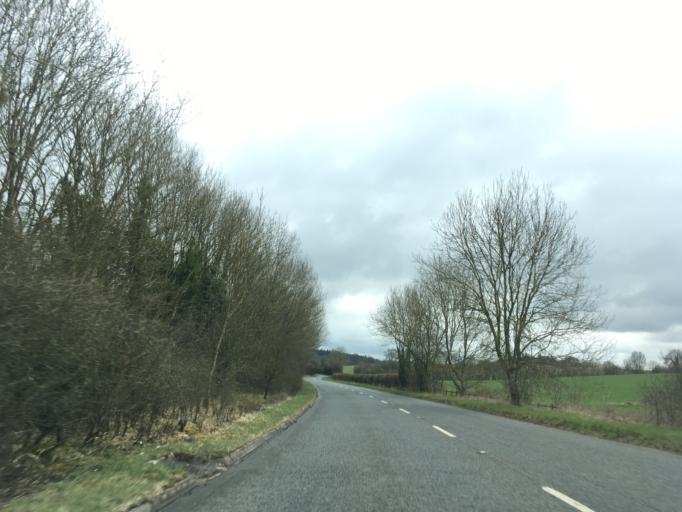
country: GB
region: England
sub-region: Wiltshire
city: Chilton Foliat
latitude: 51.4688
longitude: -1.5304
